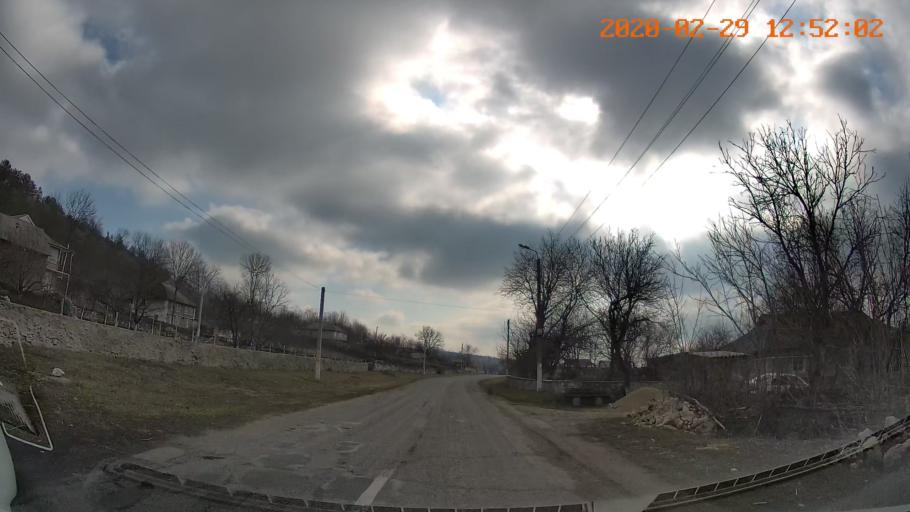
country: MD
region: Telenesti
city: Camenca
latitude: 48.1149
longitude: 28.7320
